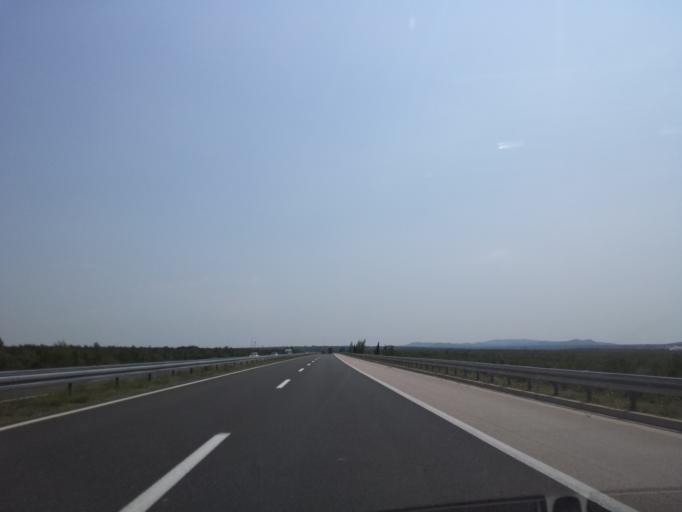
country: HR
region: Zadarska
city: Benkovac
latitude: 44.0297
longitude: 15.5658
